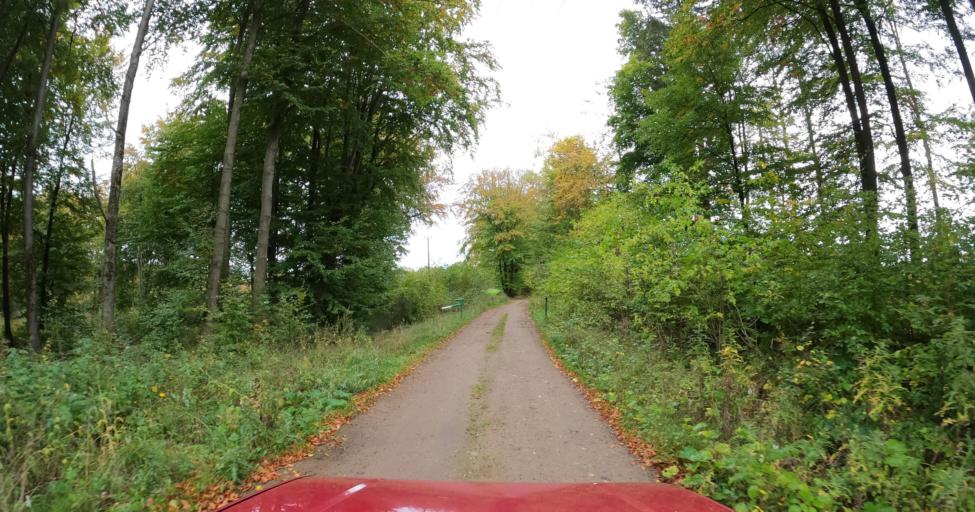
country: PL
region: West Pomeranian Voivodeship
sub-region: Powiat koszalinski
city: Polanow
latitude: 54.1150
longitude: 16.5249
